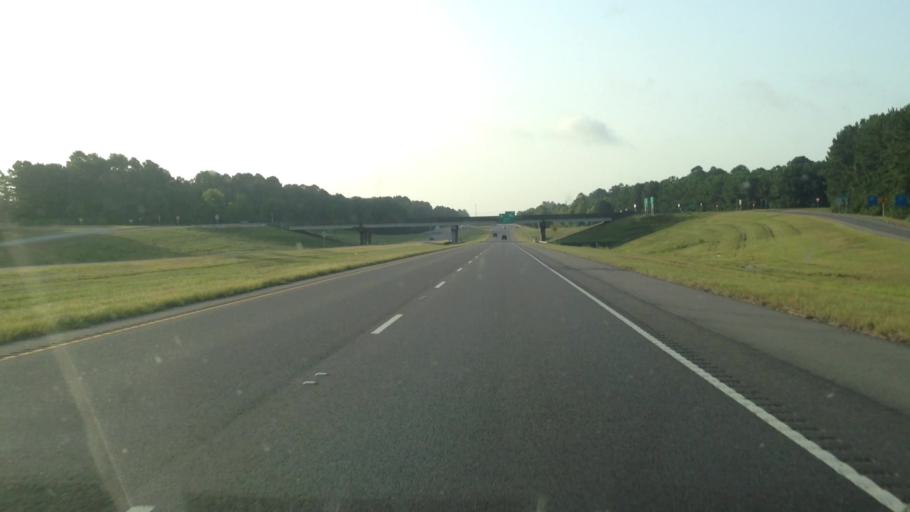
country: US
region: Louisiana
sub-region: Rapides Parish
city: Boyce
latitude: 31.4111
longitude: -92.7194
